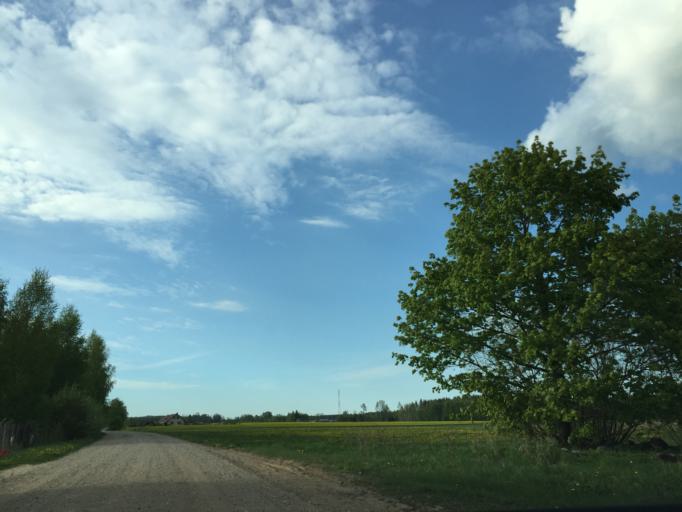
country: LV
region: Limbazu Rajons
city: Limbazi
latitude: 57.3662
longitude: 24.6931
